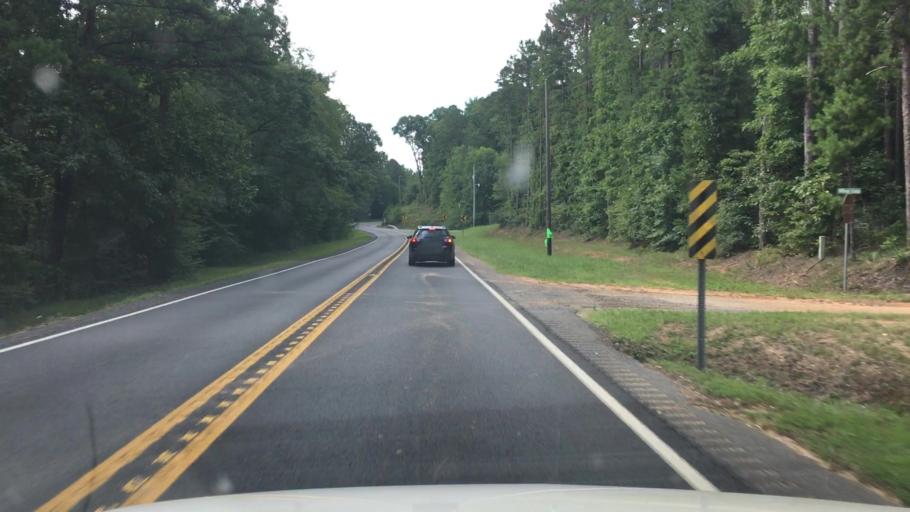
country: US
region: Arkansas
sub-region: Garland County
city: Lake Hamilton
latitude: 34.3454
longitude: -93.1842
